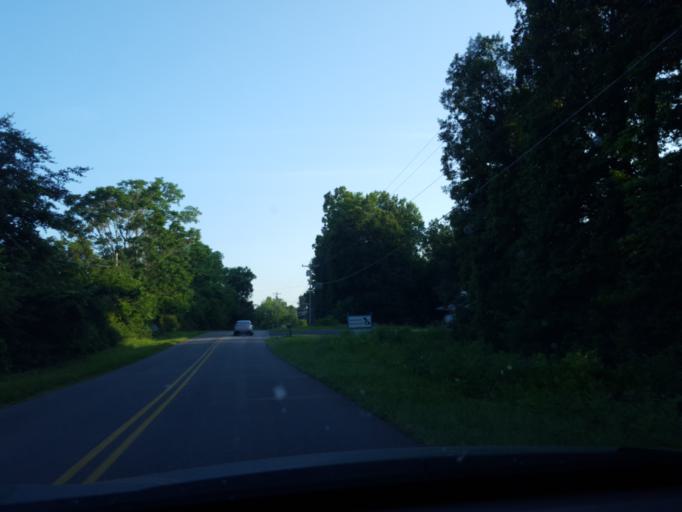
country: US
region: Virginia
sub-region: Augusta County
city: Lyndhurst
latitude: 38.0126
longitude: -78.9494
